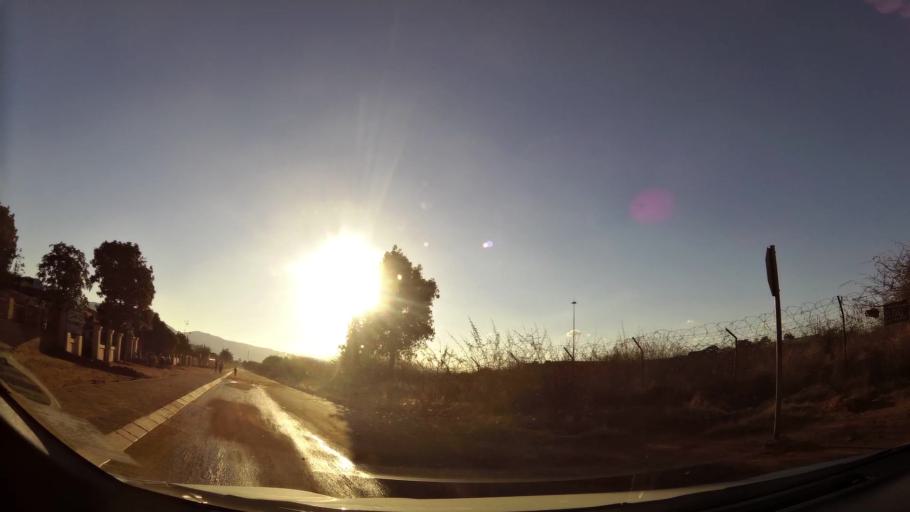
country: ZA
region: Limpopo
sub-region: Waterberg District Municipality
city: Mokopane
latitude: -24.1514
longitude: 28.9942
